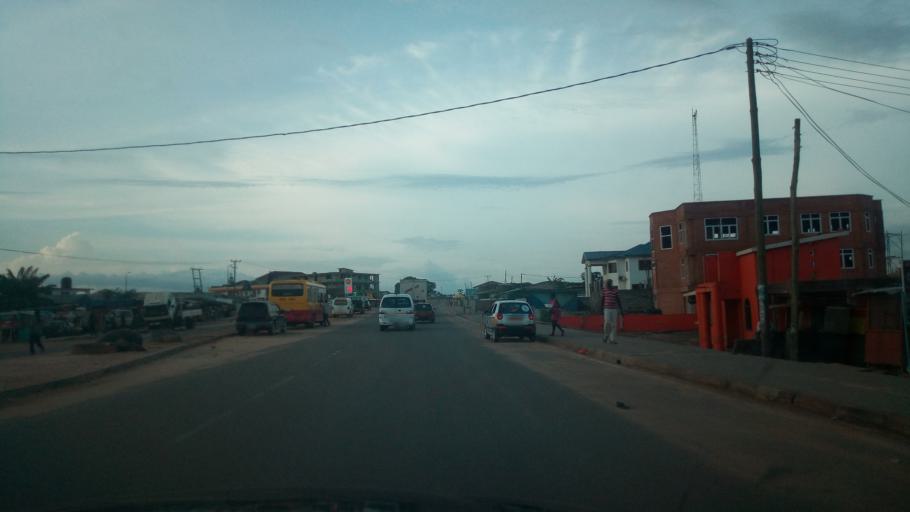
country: GH
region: Western
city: Takoradi
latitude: 4.9127
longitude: -1.7937
